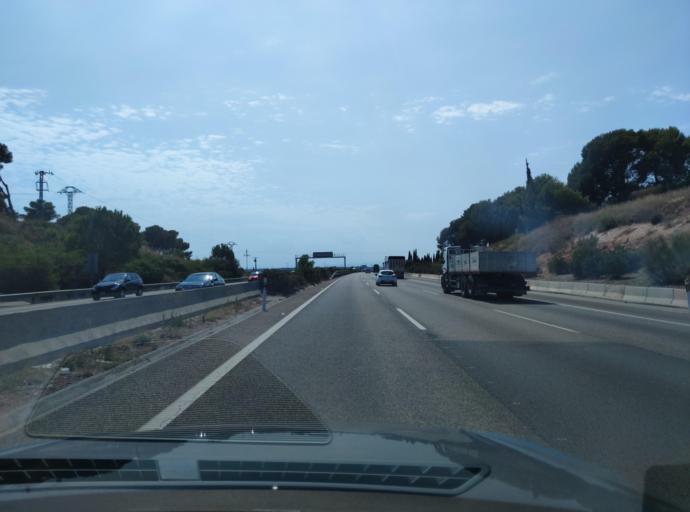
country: ES
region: Valencia
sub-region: Provincia de Valencia
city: Alfara del Patriarca
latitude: 39.5865
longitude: -0.3944
